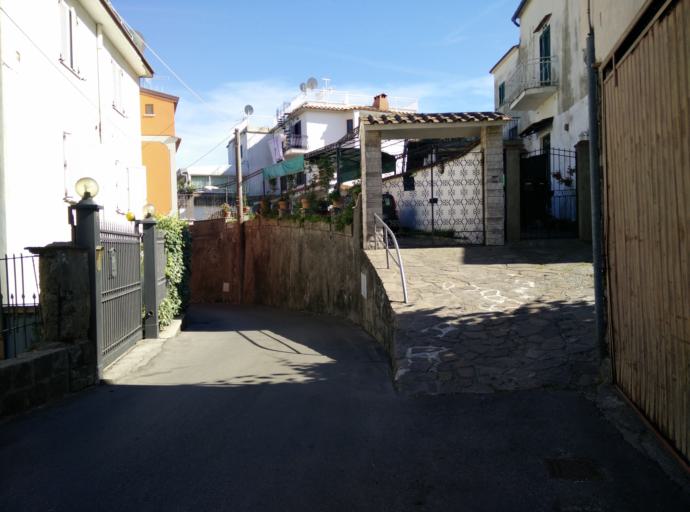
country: IT
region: Campania
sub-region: Provincia di Napoli
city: Massa Lubrense
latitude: 40.5994
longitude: 14.3848
